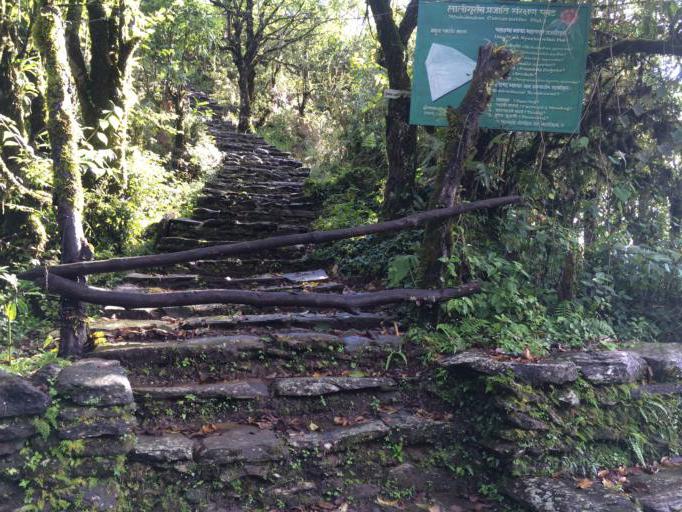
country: NP
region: Western Region
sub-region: Gandaki Zone
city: Pokhara
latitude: 28.2504
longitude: 83.8218
